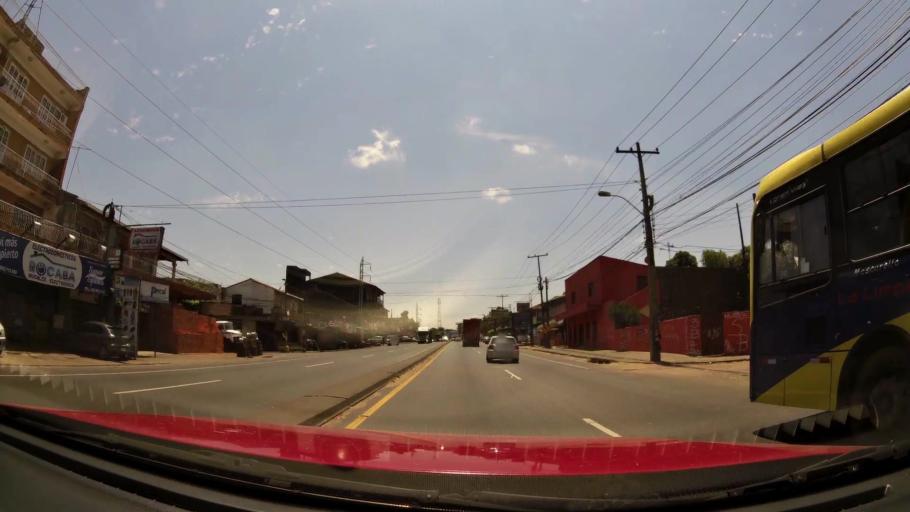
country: PY
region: Central
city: Villa Elisa
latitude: -25.3520
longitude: -57.5723
